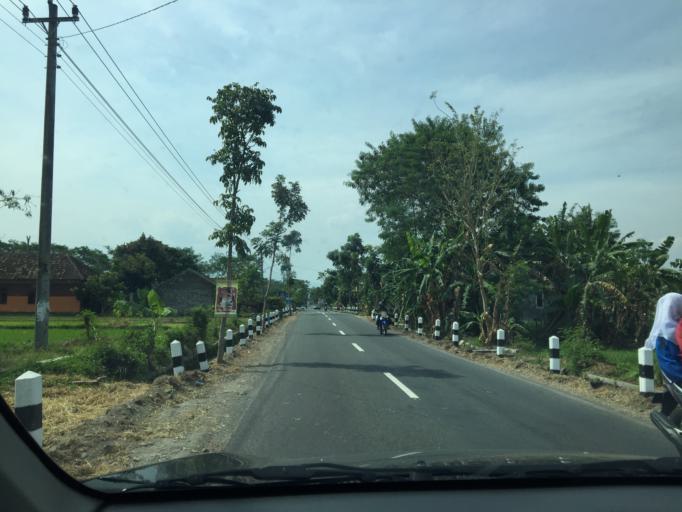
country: ID
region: Central Java
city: Candi Prambanan
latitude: -7.7482
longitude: 110.4812
